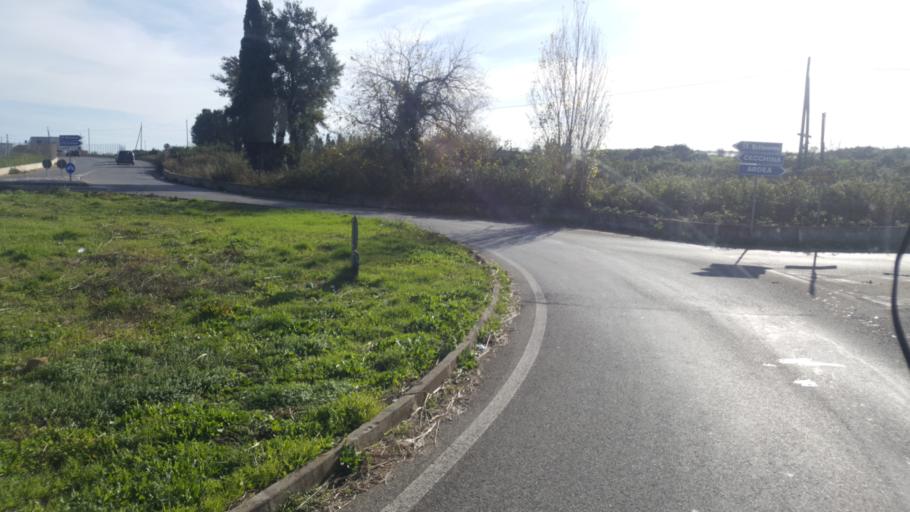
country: IT
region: Latium
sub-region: Citta metropolitana di Roma Capitale
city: Mantiglia di Ardea
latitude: 41.6702
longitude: 12.6369
